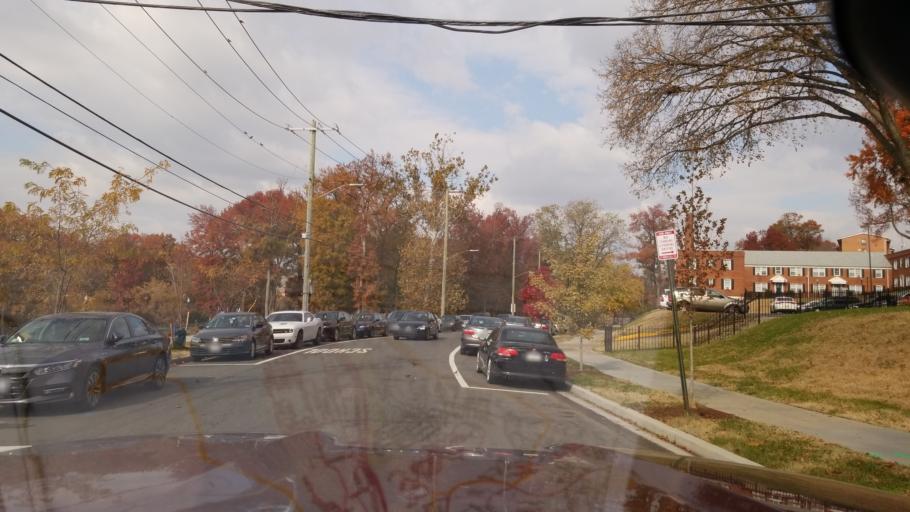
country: US
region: Maryland
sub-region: Prince George's County
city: Glassmanor
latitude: 38.8261
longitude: -77.0028
